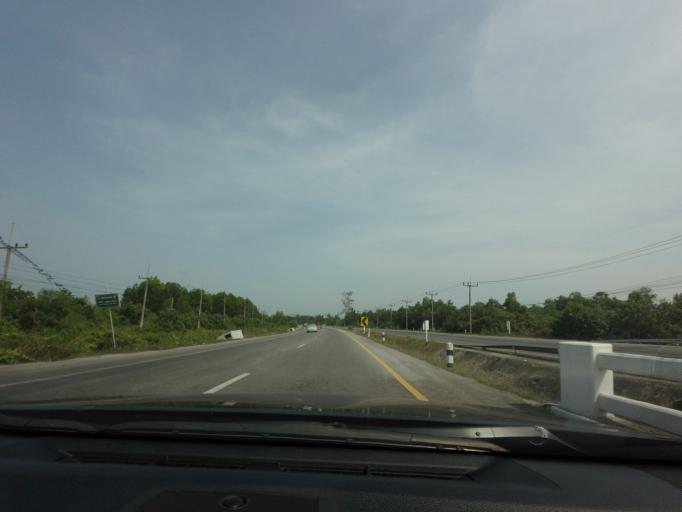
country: TH
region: Pattani
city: Yaring
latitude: 6.8267
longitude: 101.3935
